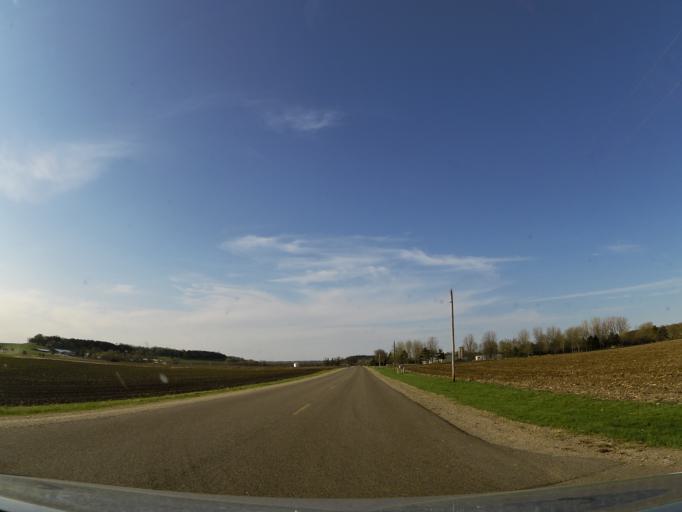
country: US
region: Wisconsin
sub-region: Pierce County
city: River Falls
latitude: 44.8118
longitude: -92.6448
